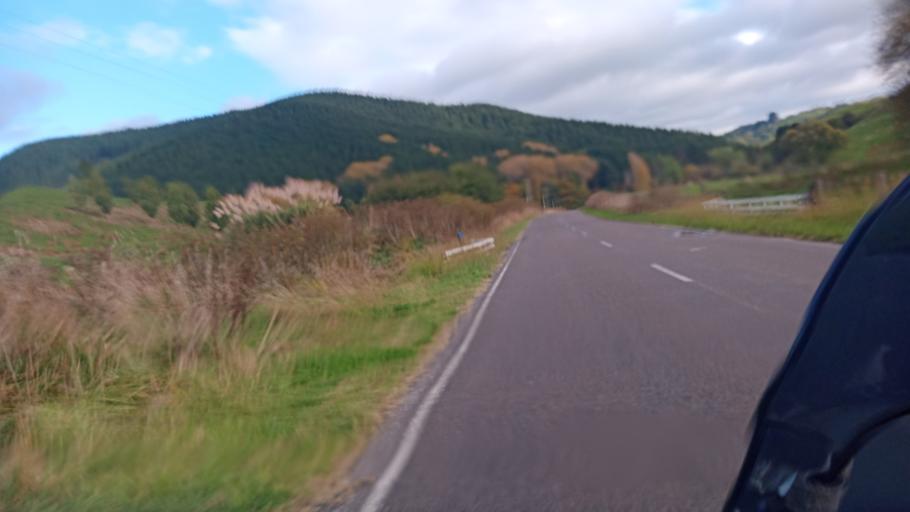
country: NZ
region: Gisborne
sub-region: Gisborne District
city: Gisborne
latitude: -38.5714
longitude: 177.7287
